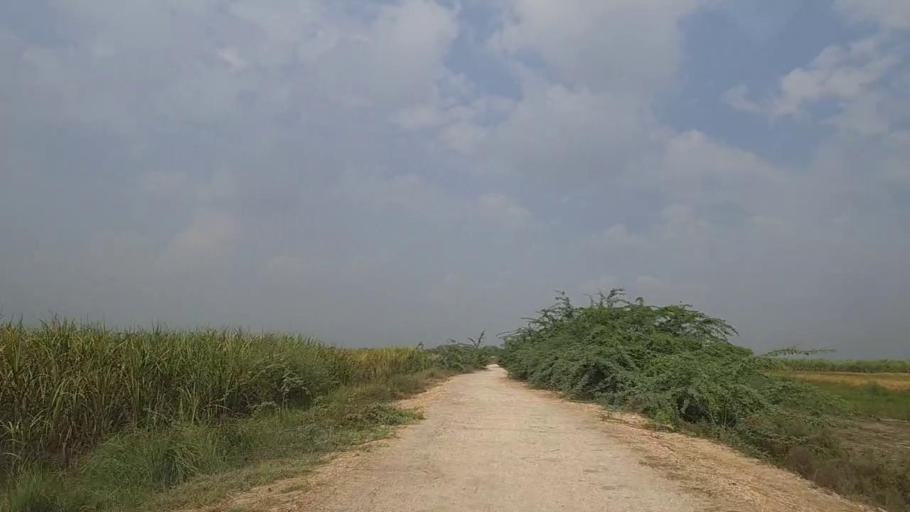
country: PK
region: Sindh
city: Daro Mehar
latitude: 24.6925
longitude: 68.1264
